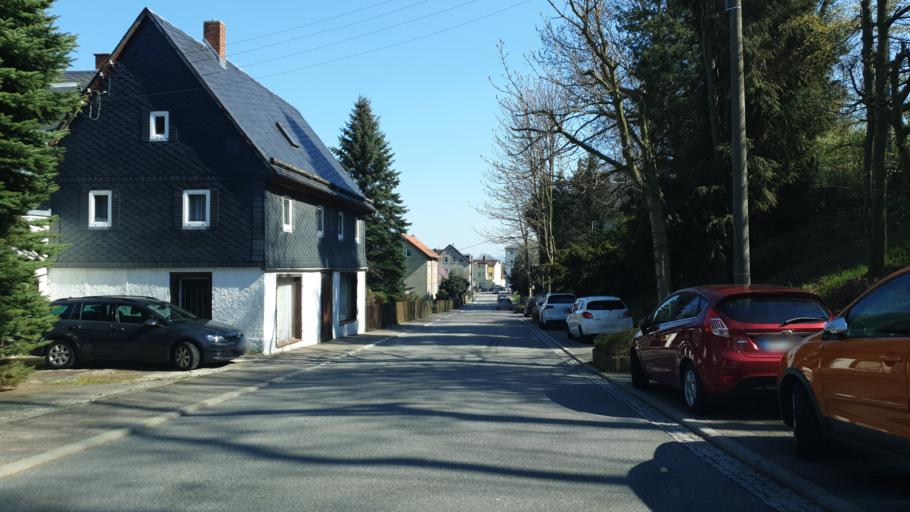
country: DE
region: Saxony
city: Hohenstein-Ernstthal
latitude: 50.8096
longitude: 12.7495
